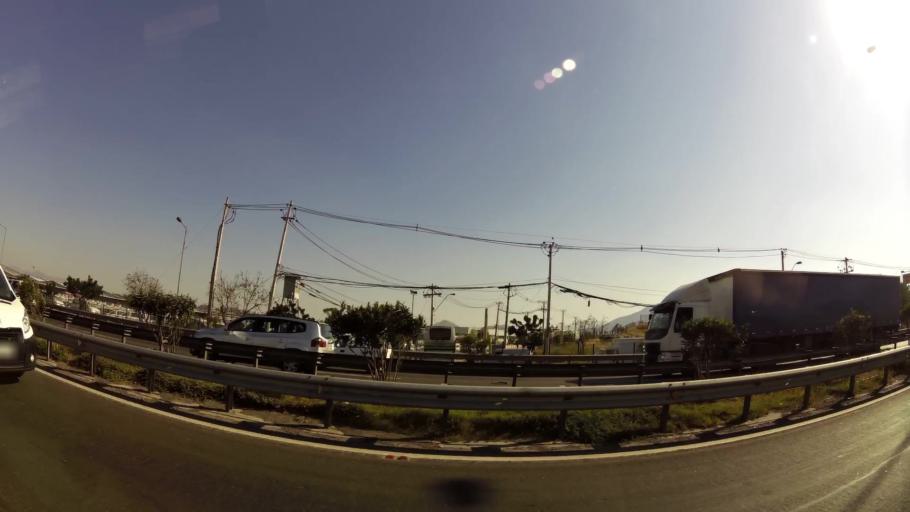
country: CL
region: Santiago Metropolitan
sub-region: Provincia de Santiago
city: Lo Prado
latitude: -33.4514
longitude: -70.7728
